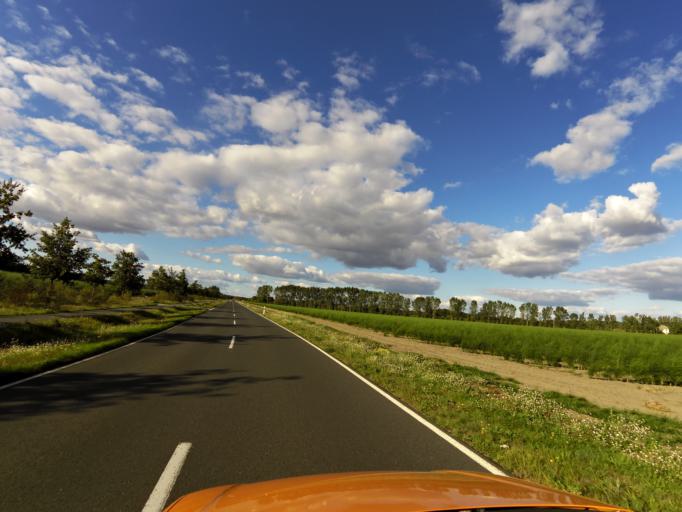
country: DE
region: Brandenburg
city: Luckenwalde
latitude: 52.1468
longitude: 13.1859
